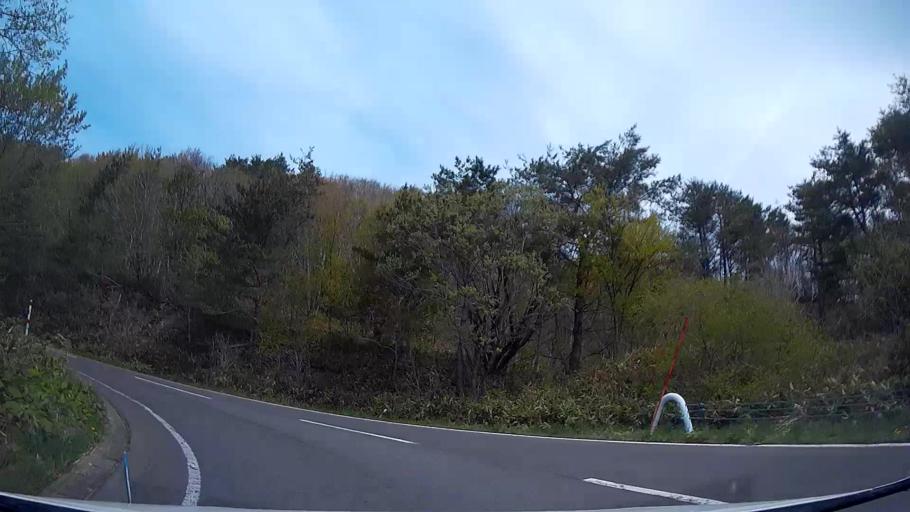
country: JP
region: Iwate
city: Shizukuishi
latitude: 39.9251
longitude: 140.9685
